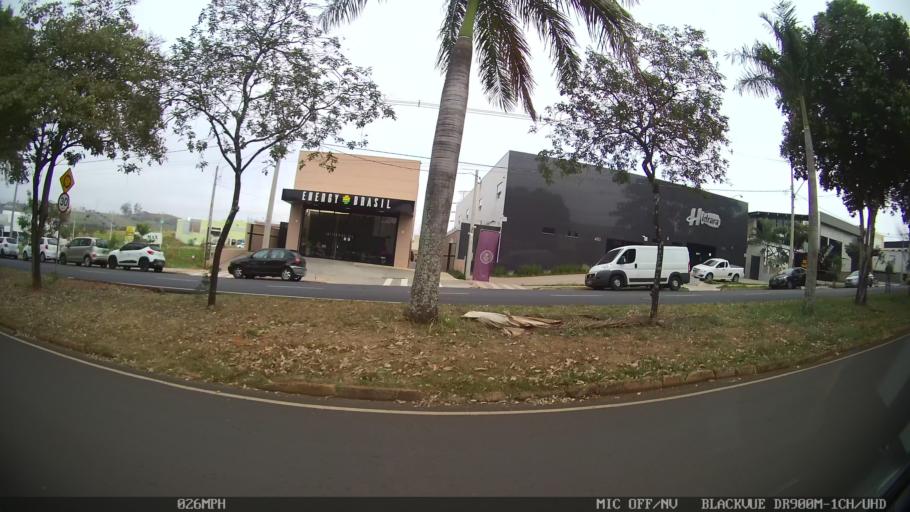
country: BR
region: Sao Paulo
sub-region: Sao Jose Do Rio Preto
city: Sao Jose do Rio Preto
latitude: -20.8450
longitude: -49.3702
